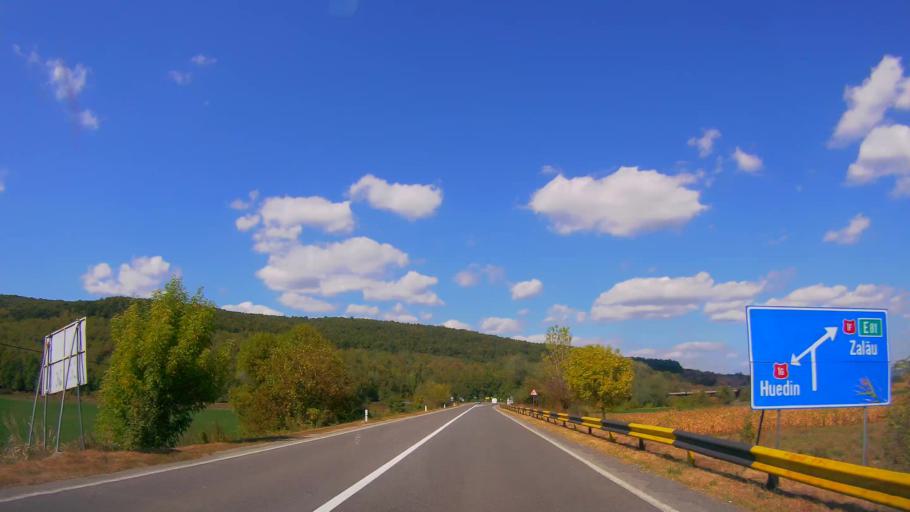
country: RO
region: Salaj
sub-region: Comuna Zimbor
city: Zimbor
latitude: 46.9928
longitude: 23.2506
